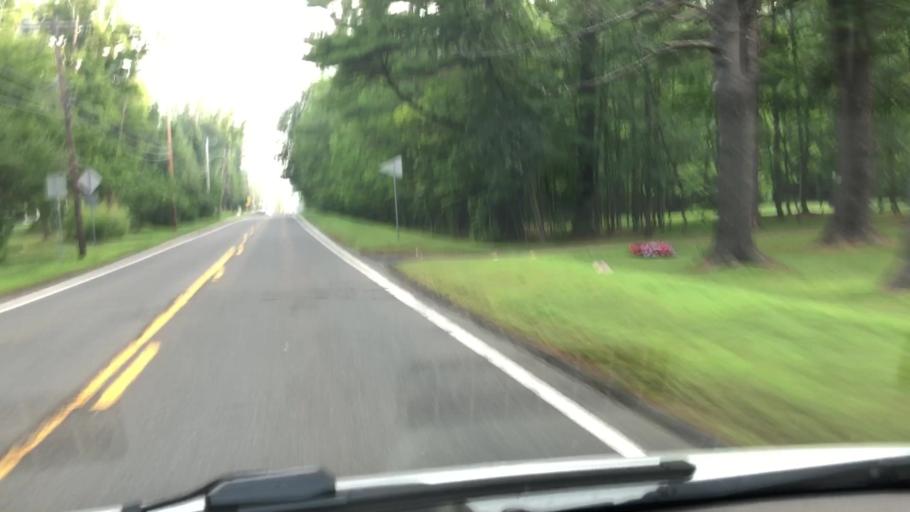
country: US
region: Massachusetts
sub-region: Hampshire County
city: Chesterfield
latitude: 42.4379
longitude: -72.7986
